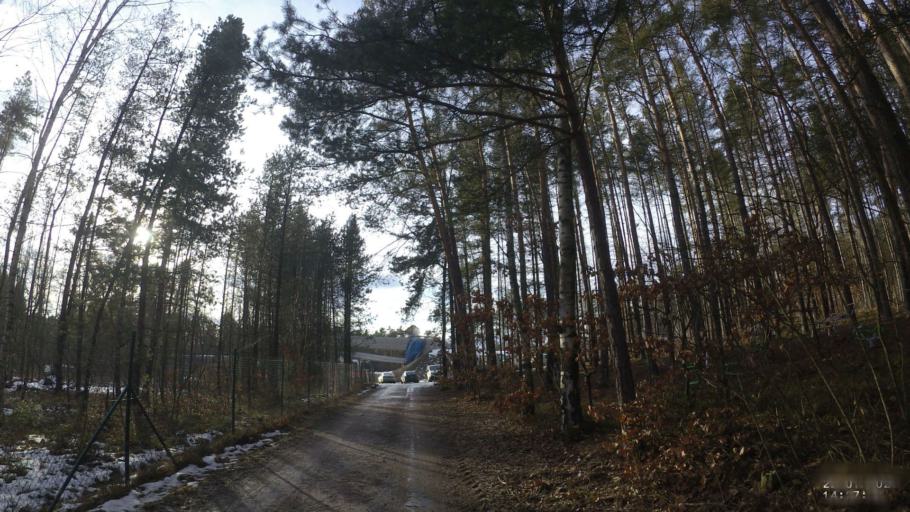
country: CZ
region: Plzensky
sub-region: Okres Plzen-Sever
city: Tremosna
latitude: 49.7902
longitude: 13.3859
